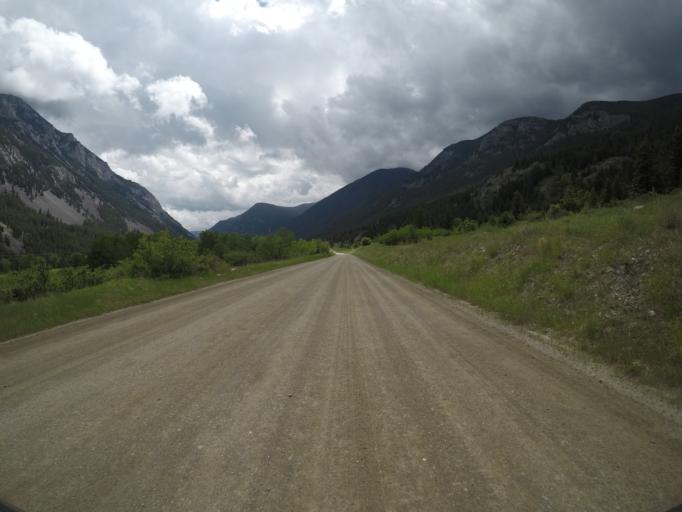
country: US
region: Montana
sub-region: Park County
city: Livingston
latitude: 45.5189
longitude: -110.2257
